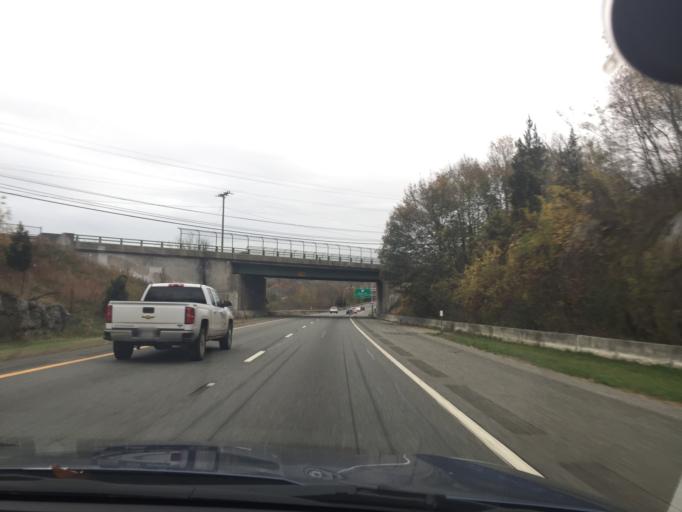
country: US
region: Rhode Island
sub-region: Providence County
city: Cranston
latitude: 41.7665
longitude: -71.4831
